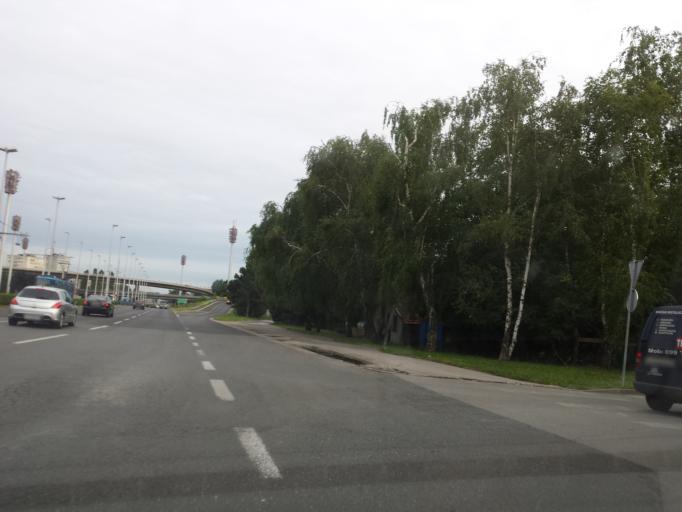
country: HR
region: Grad Zagreb
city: Novi Zagreb
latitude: 45.7984
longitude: 15.9973
